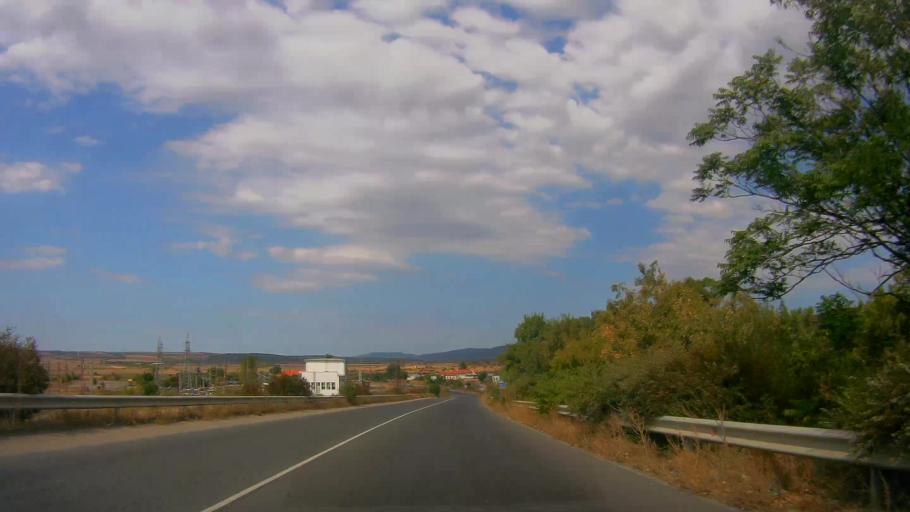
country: BG
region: Burgas
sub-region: Obshtina Aytos
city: Aytos
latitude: 42.7045
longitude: 27.2399
